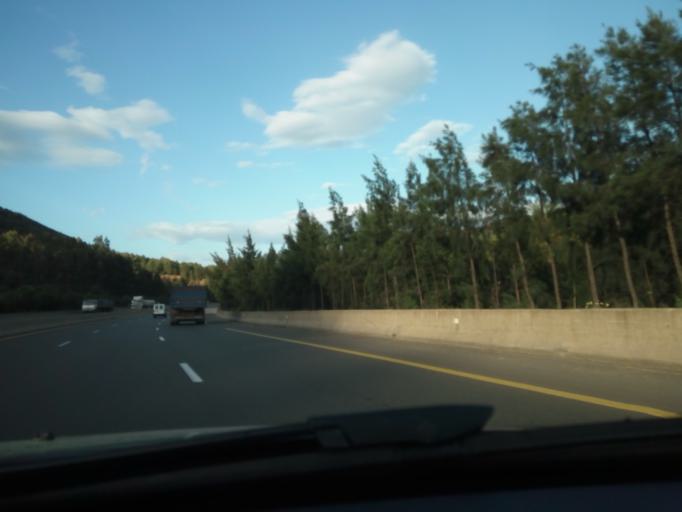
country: DZ
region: Tipaza
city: El Affroun
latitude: 36.3927
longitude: 2.5242
